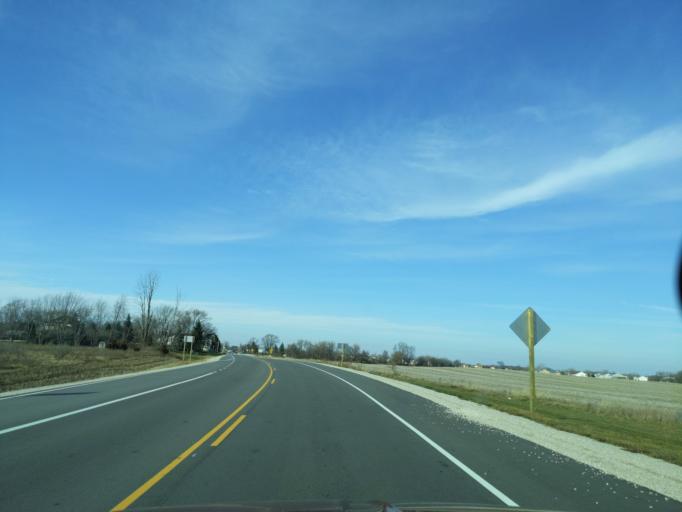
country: US
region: Wisconsin
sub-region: Walworth County
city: Whitewater
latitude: 42.8225
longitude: -88.7009
